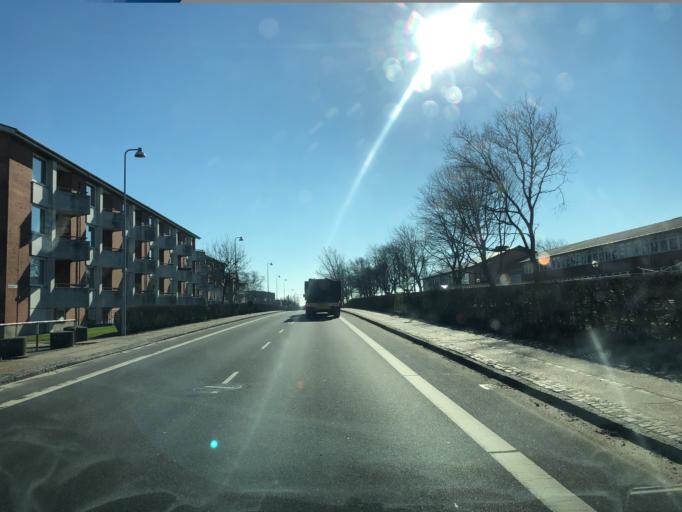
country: DK
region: Central Jutland
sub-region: Ikast-Brande Kommune
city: Ikast
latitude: 56.1390
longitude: 9.1645
